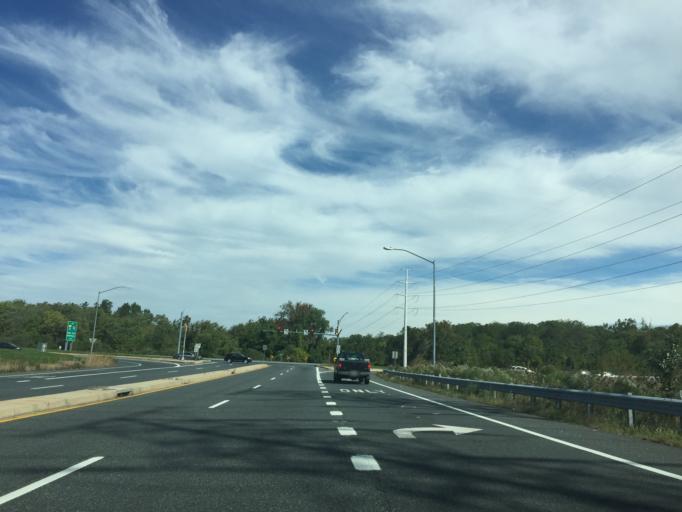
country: US
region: Maryland
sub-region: Baltimore County
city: White Marsh
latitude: 39.3719
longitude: -76.4316
